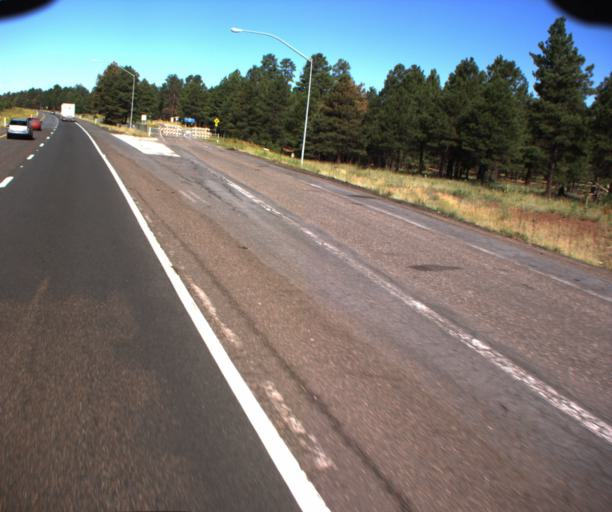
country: US
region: Arizona
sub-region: Coconino County
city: Parks
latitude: 35.2497
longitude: -111.8643
